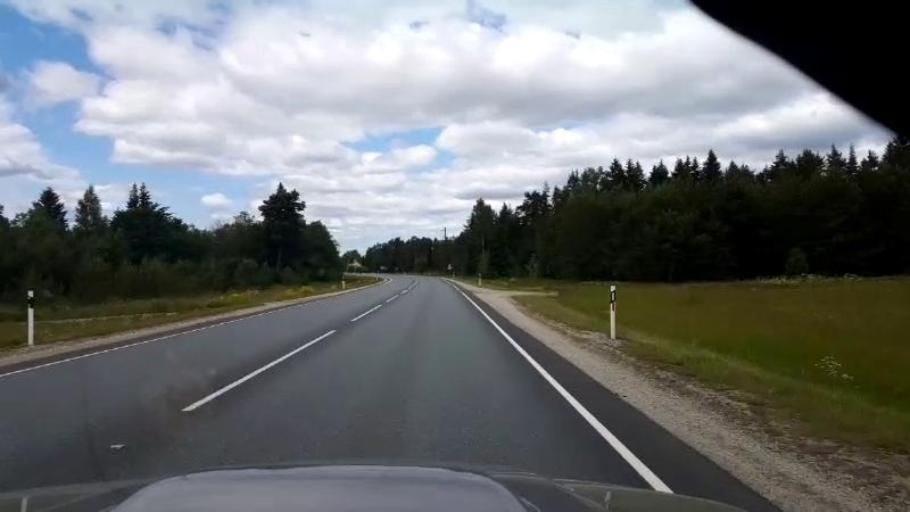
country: EE
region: Raplamaa
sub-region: Maerjamaa vald
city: Marjamaa
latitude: 58.9757
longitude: 24.4750
